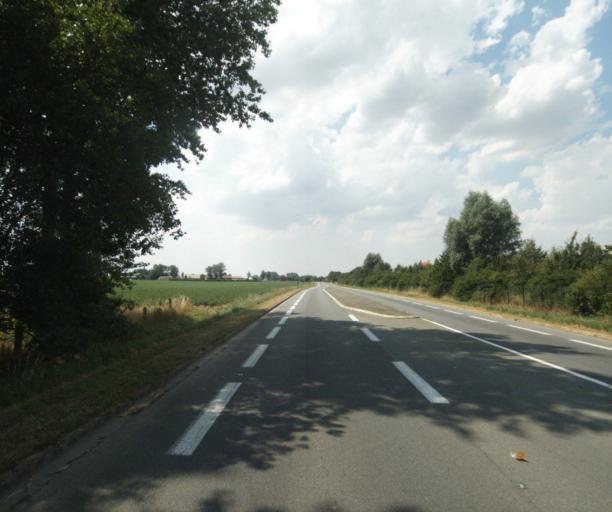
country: FR
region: Nord-Pas-de-Calais
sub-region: Departement du Nord
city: Comines
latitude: 50.7508
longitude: 2.9941
